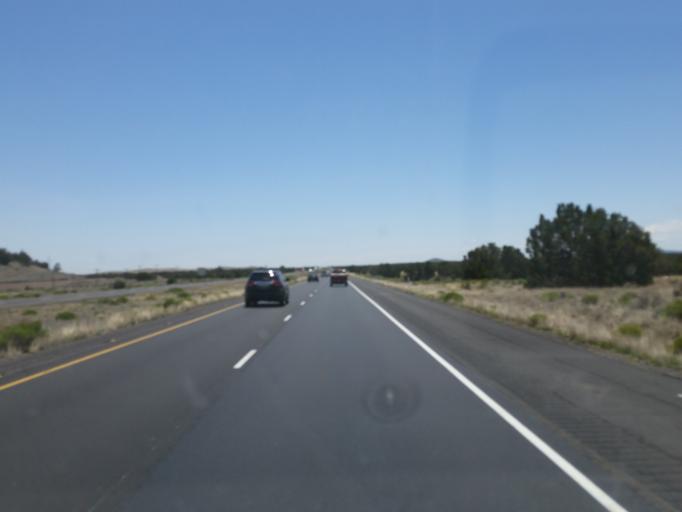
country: US
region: Arizona
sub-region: Coconino County
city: Flagstaff
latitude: 35.1948
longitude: -111.3904
